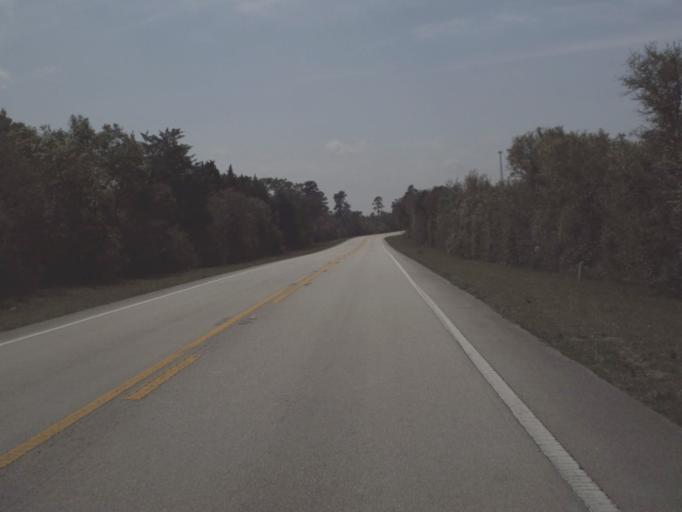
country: US
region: Florida
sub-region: Lake County
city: Astor
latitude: 29.2239
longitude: -81.6461
